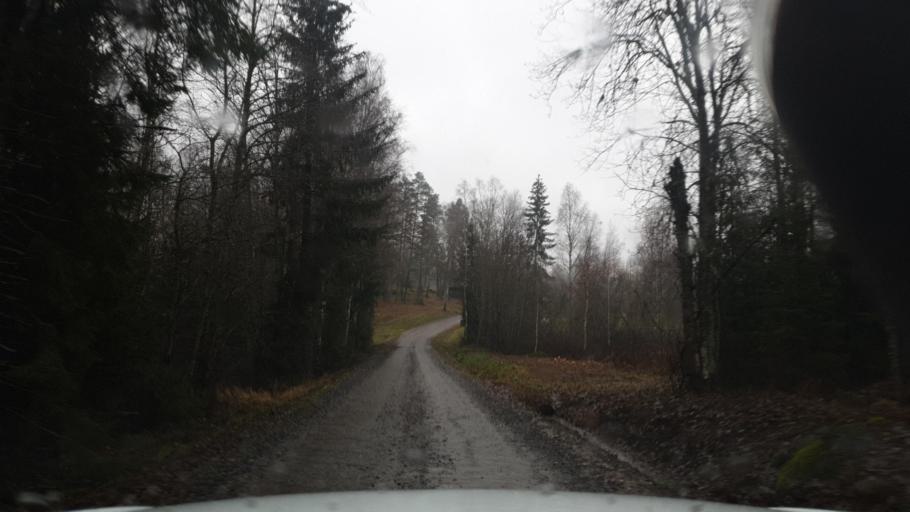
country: SE
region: Vaermland
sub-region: Karlstads Kommun
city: Edsvalla
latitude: 59.4701
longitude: 13.1272
